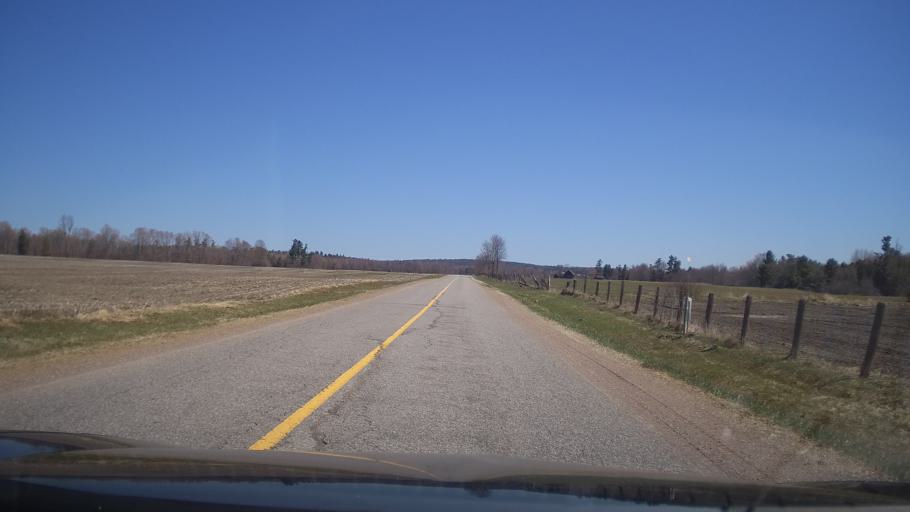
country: CA
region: Quebec
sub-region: Outaouais
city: Shawville
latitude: 45.5404
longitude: -76.3926
